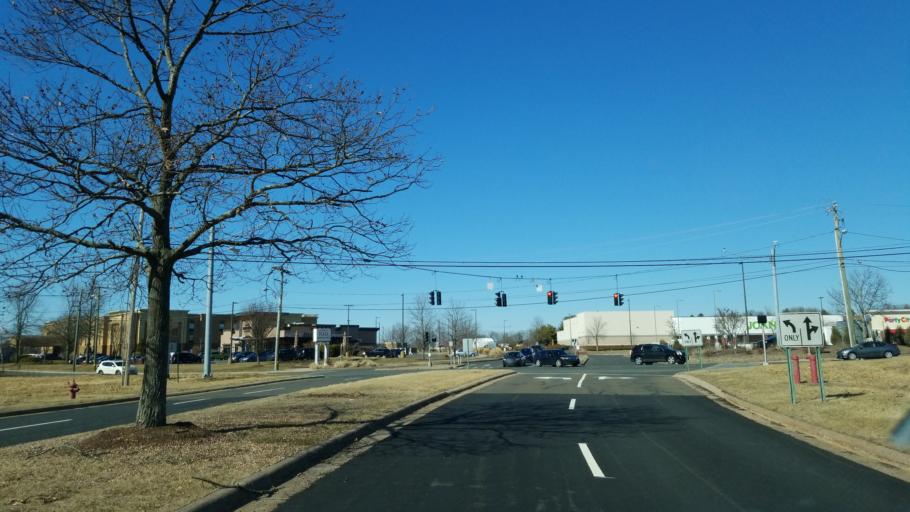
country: US
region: Connecticut
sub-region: Hartford County
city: Manchester
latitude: 41.8036
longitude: -72.5623
